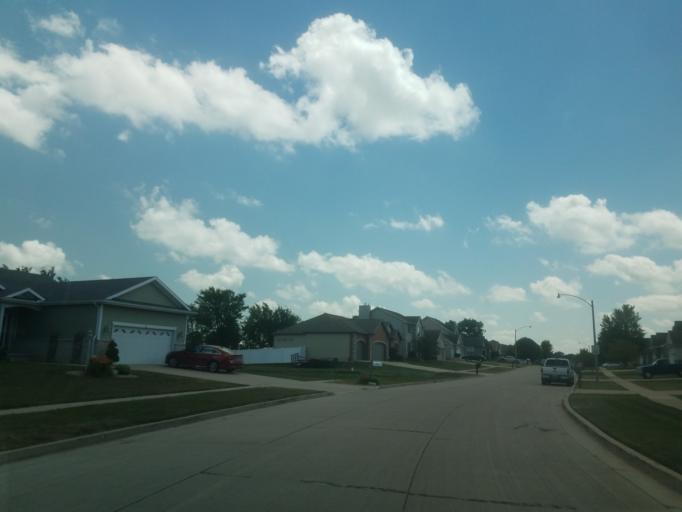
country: US
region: Illinois
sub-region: McLean County
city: Bloomington
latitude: 40.4570
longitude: -89.0331
